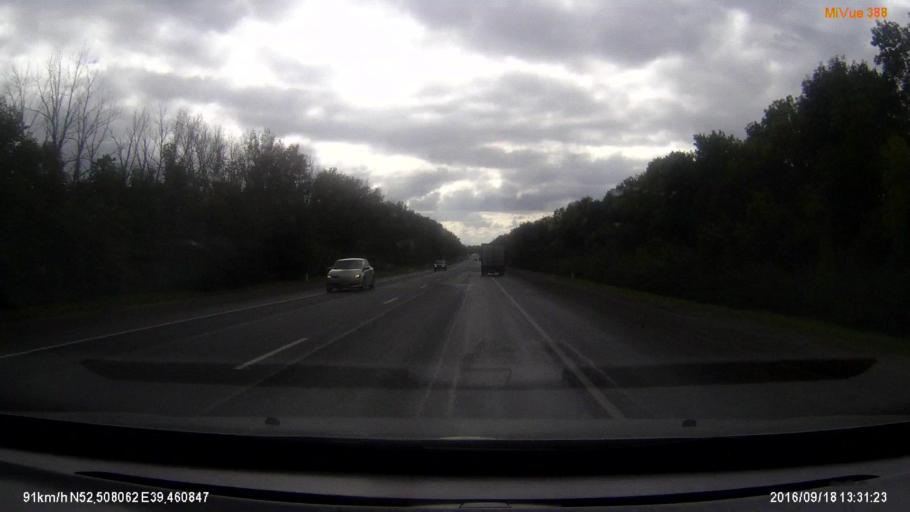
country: RU
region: Lipetsk
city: Borinskoye
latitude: 52.4656
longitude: 39.4044
